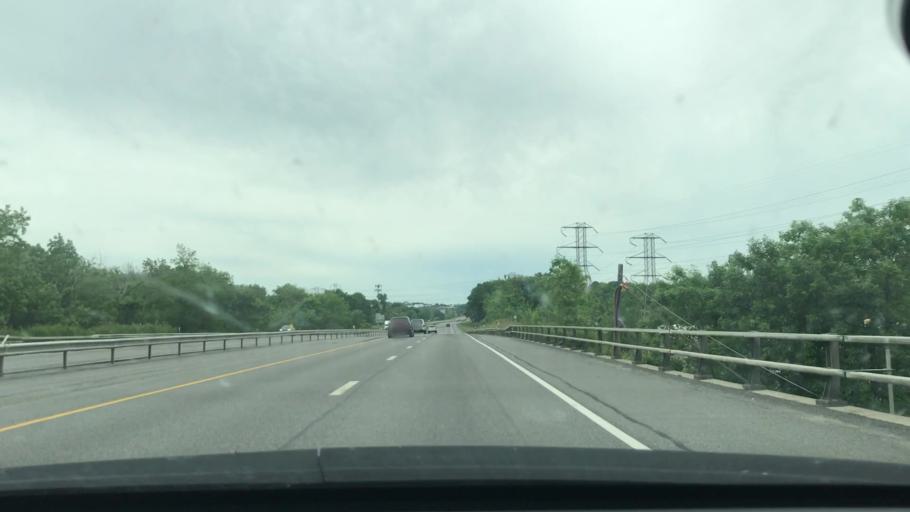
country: US
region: New York
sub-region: Onondaga County
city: Lakeland
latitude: 43.1163
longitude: -76.2439
